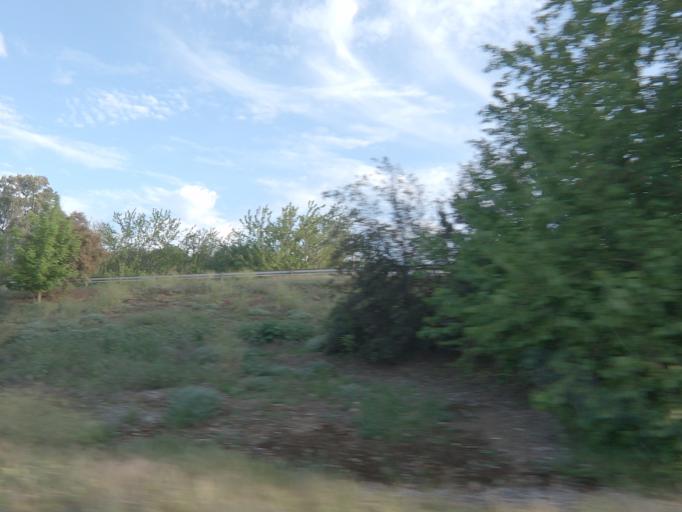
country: ES
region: Extremadura
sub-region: Provincia de Badajoz
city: Torremayor
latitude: 38.8612
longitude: -6.5447
